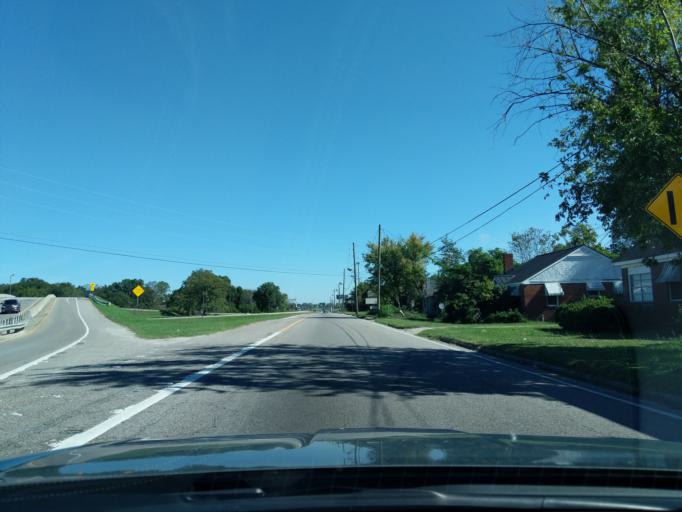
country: US
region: Georgia
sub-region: Richmond County
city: Augusta
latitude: 33.4362
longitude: -82.0068
